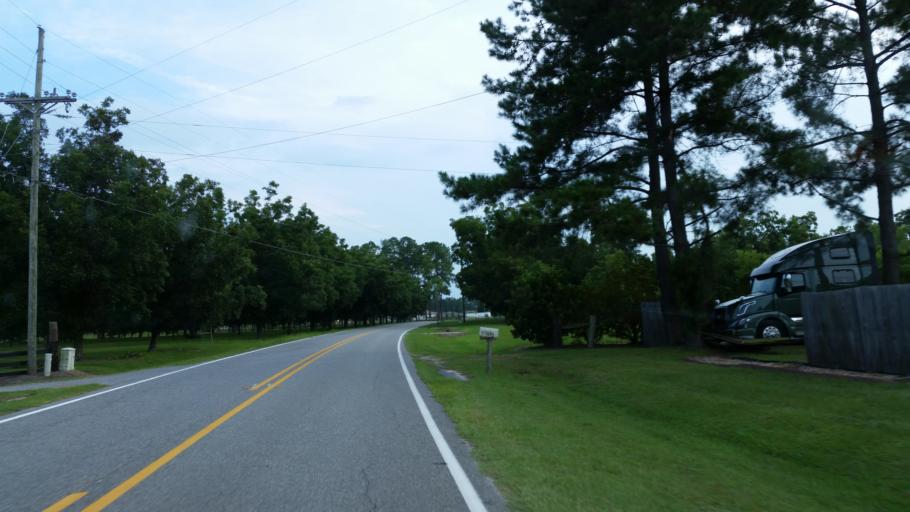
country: US
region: Georgia
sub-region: Lowndes County
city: Hahira
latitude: 31.0020
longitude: -83.3871
